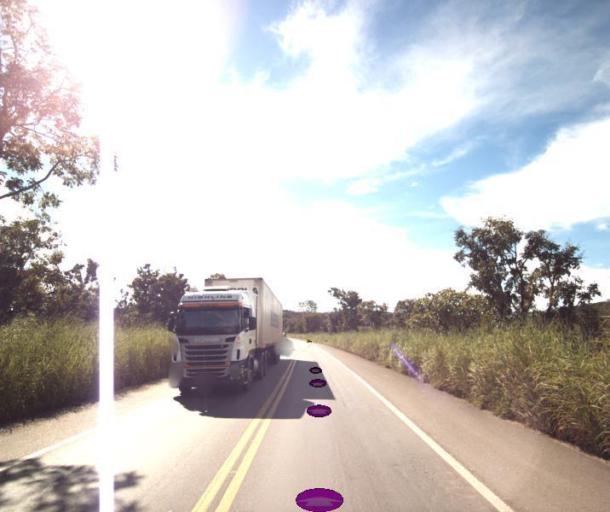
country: BR
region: Goias
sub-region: Uruana
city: Uruana
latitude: -15.4983
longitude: -49.4832
